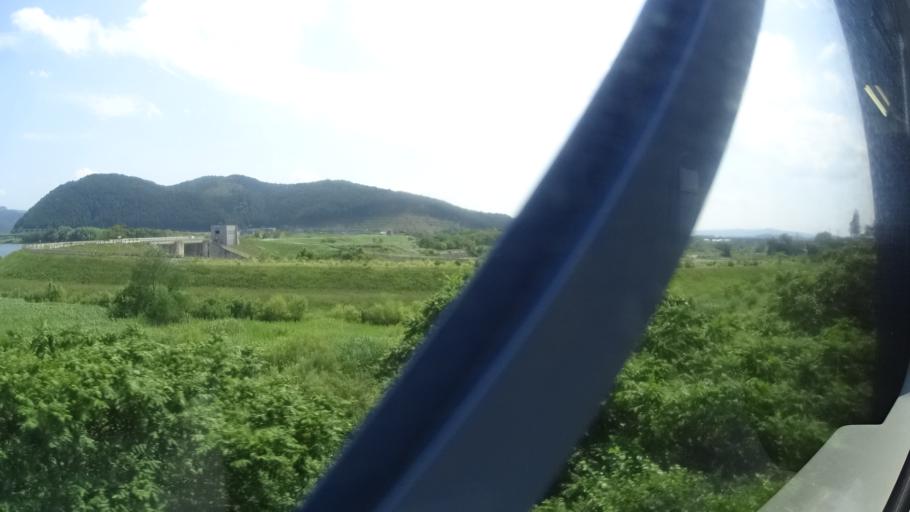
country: JP
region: Miyagi
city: Wakuya
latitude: 38.6086
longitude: 141.2944
